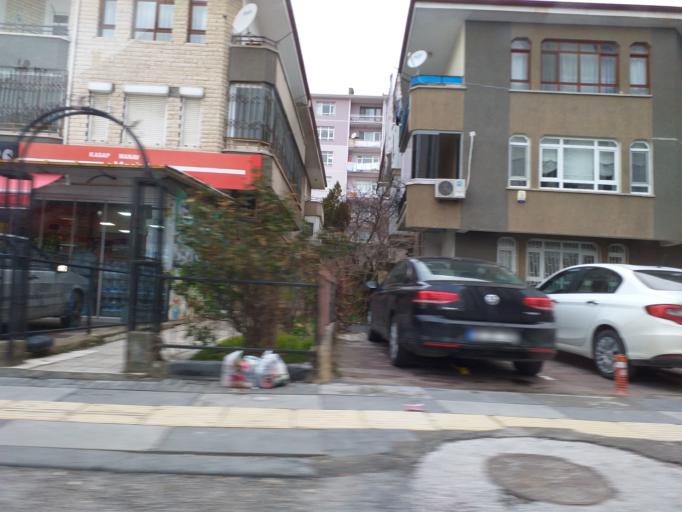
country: TR
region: Ankara
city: Ankara
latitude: 39.9798
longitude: 32.8214
